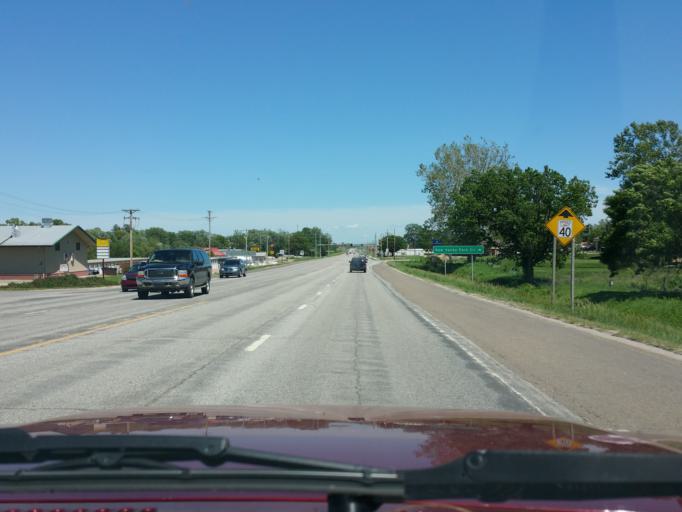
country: US
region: Kansas
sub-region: Pottawatomie County
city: Wamego
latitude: 39.2102
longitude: -96.3191
